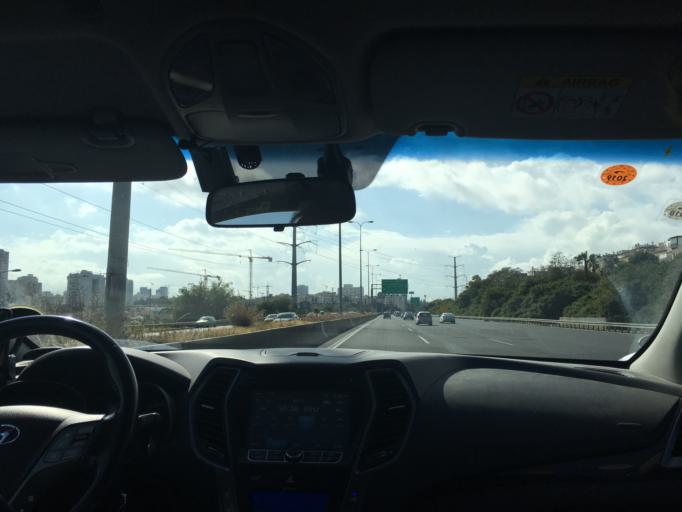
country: IL
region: Tel Aviv
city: Giv`at Shemu'el
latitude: 32.0880
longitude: 34.8458
